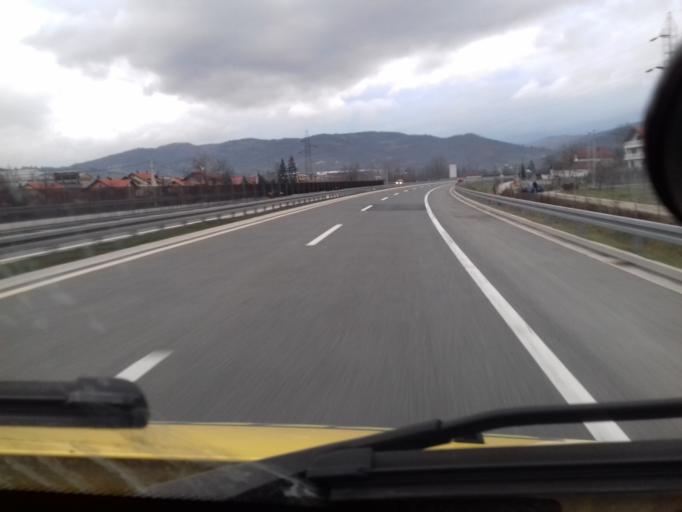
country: BA
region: Federation of Bosnia and Herzegovina
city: Ilijas
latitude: 43.9618
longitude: 18.2583
